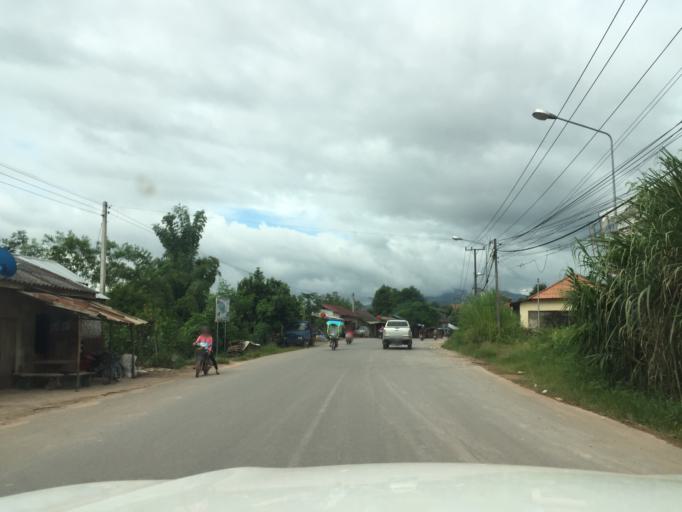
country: LA
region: Oudomxai
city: Muang Xay
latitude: 20.6986
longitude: 101.9909
